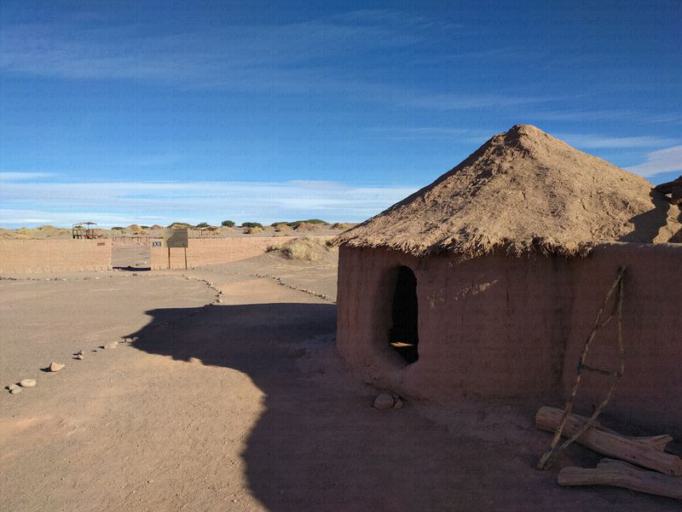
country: CL
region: Antofagasta
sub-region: Provincia de El Loa
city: San Pedro de Atacama
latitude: -22.9678
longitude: -68.2431
